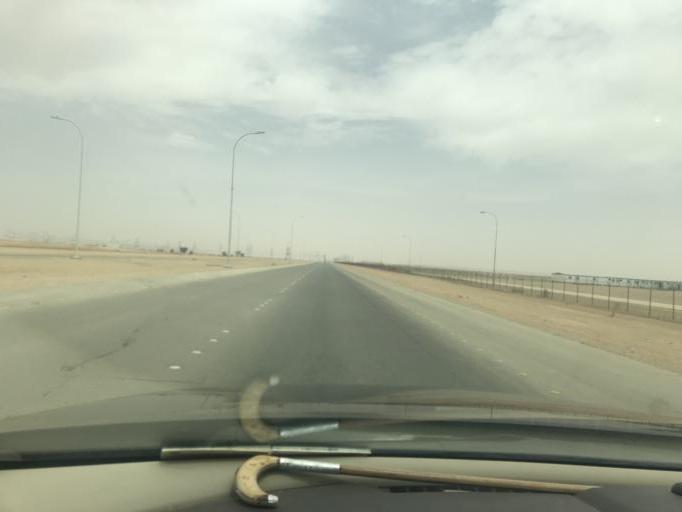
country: SA
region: Ar Riyad
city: Riyadh
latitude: 24.9634
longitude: 46.6680
